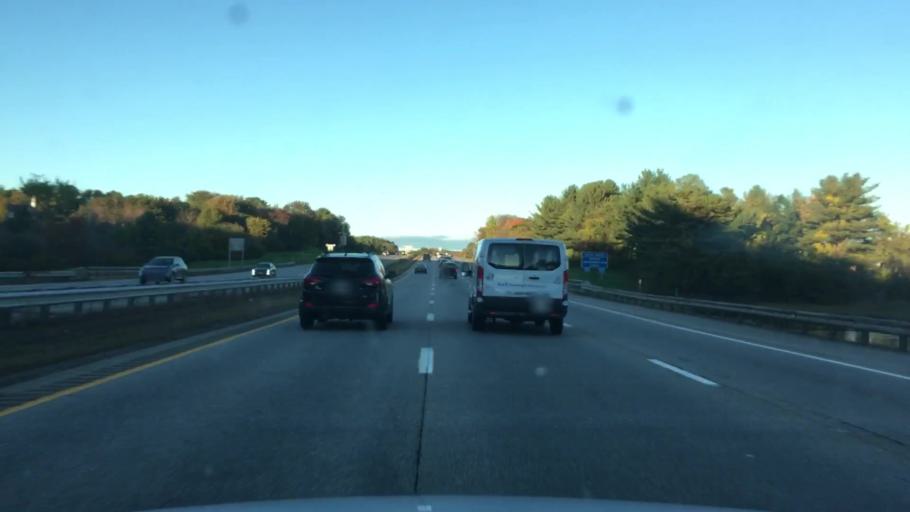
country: US
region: Maine
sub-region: York County
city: Kittery
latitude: 43.1144
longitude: -70.7348
